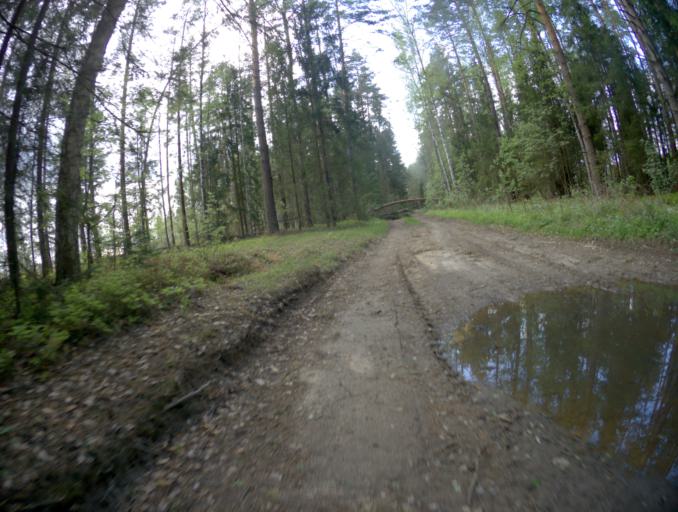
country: RU
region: Rjazan
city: Tuma
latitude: 55.2115
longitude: 40.4460
